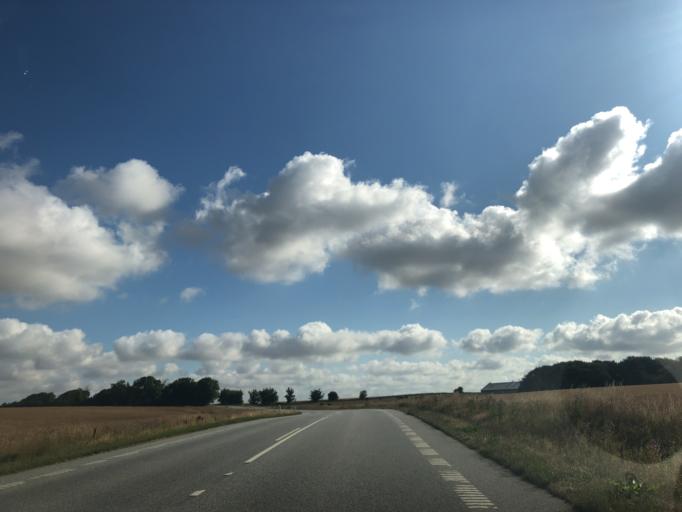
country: DK
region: Central Jutland
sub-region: Skive Kommune
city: Skive
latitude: 56.6333
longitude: 8.9171
